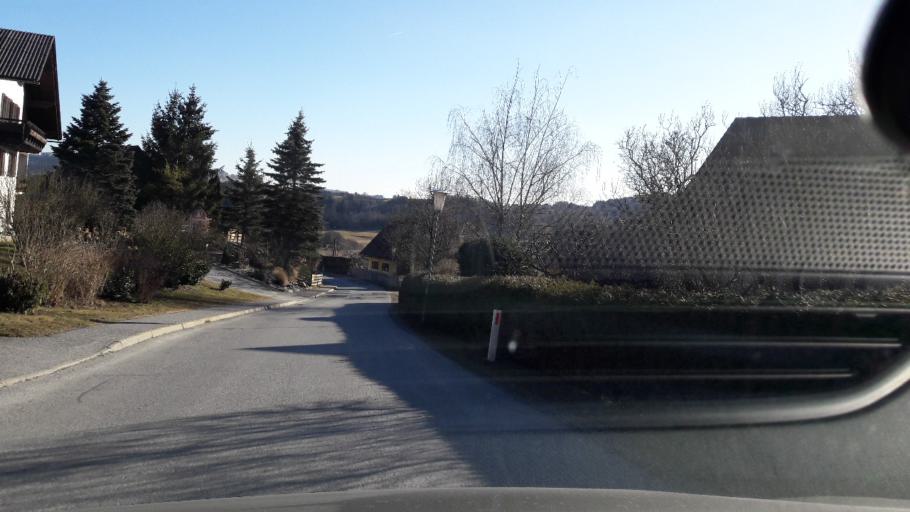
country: AT
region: Styria
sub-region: Politischer Bezirk Graz-Umgebung
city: Eisbach
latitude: 47.1314
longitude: 15.2872
